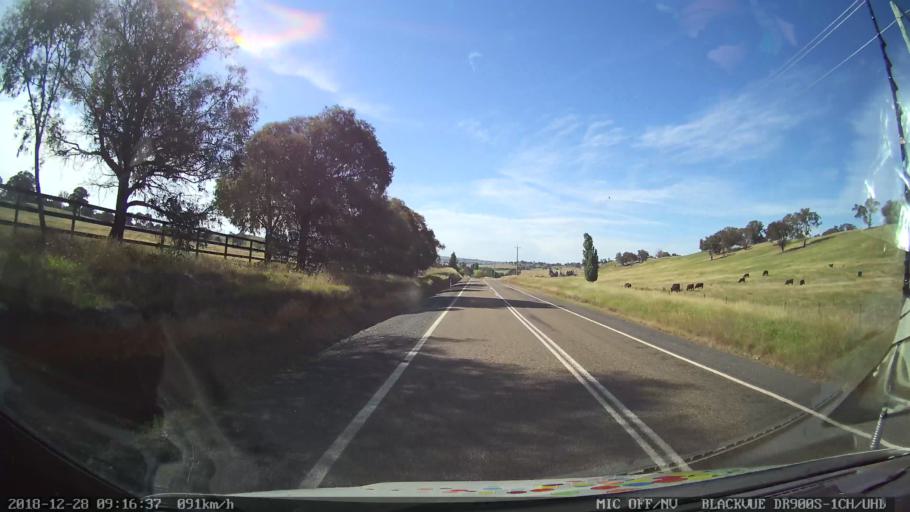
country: AU
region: New South Wales
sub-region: Upper Lachlan Shire
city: Crookwell
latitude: -34.3110
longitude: 149.3564
